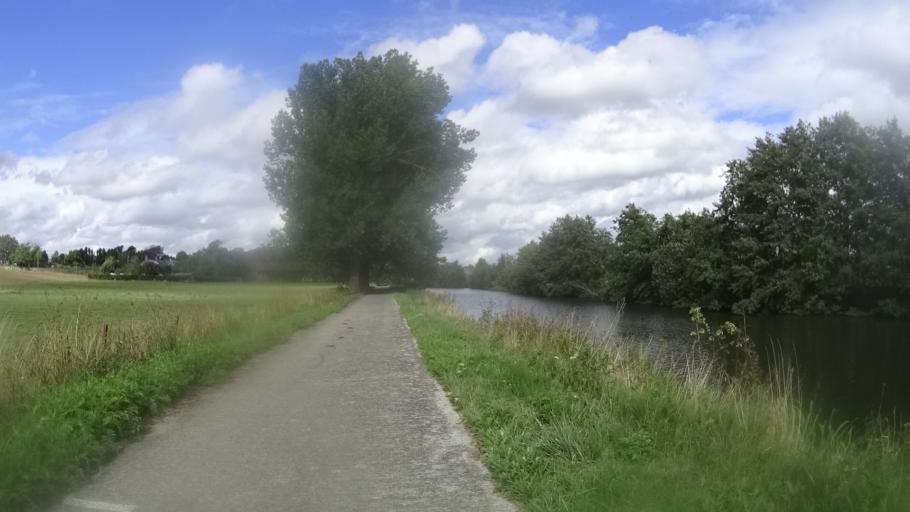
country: BE
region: Wallonia
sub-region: Province du Hainaut
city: Merbes-le-Chateau
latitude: 50.3175
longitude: 4.1510
